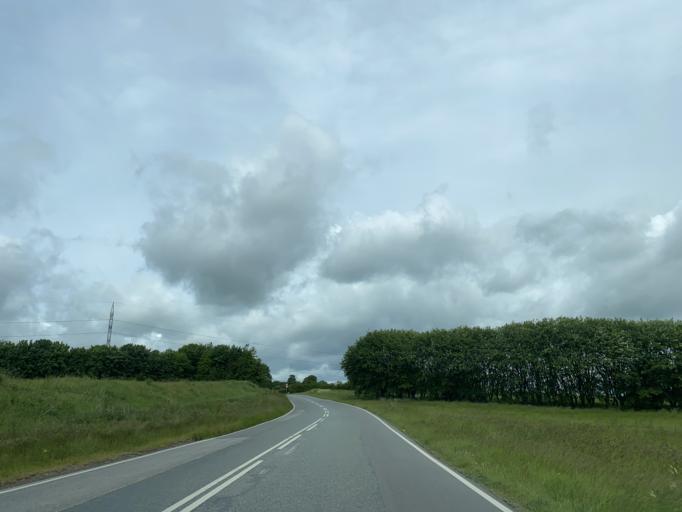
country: DK
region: Central Jutland
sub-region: Arhus Kommune
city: Trige
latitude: 56.1883
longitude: 10.1508
